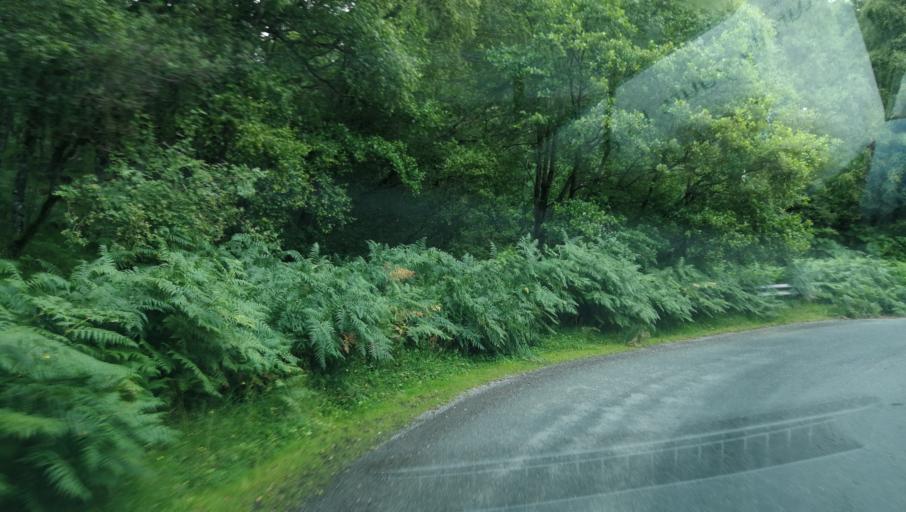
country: GB
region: Scotland
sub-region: Highland
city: Beauly
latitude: 57.3187
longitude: -4.8108
